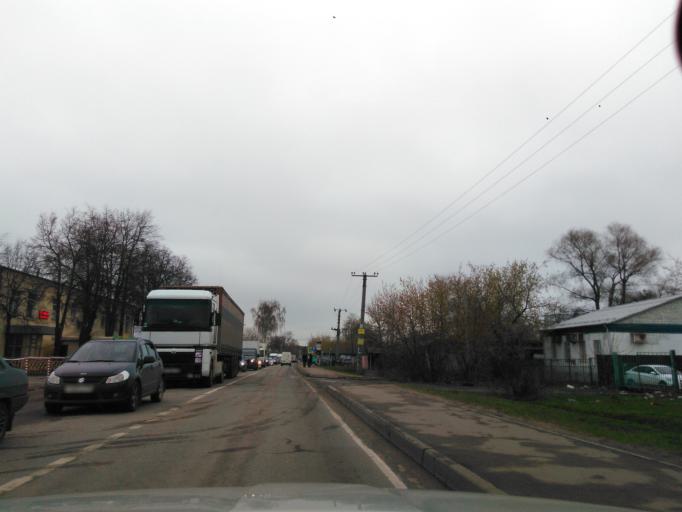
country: RU
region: Moskovskaya
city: Nakhabino
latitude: 55.8433
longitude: 37.1821
